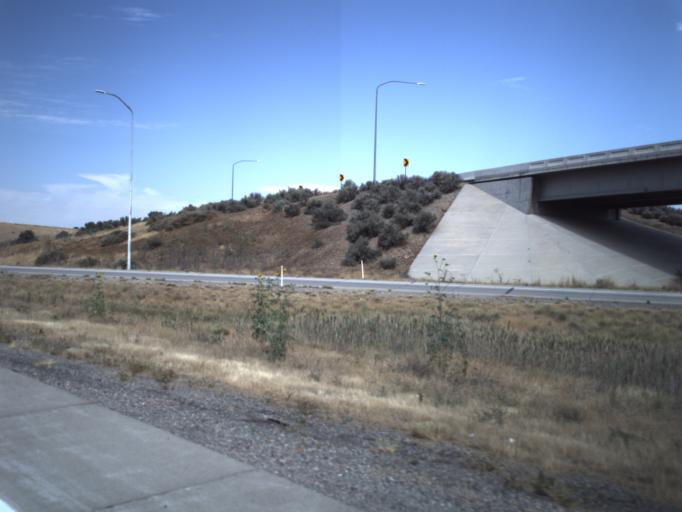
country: US
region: Utah
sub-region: Salt Lake County
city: West Valley City
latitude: 40.7652
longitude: -111.9806
